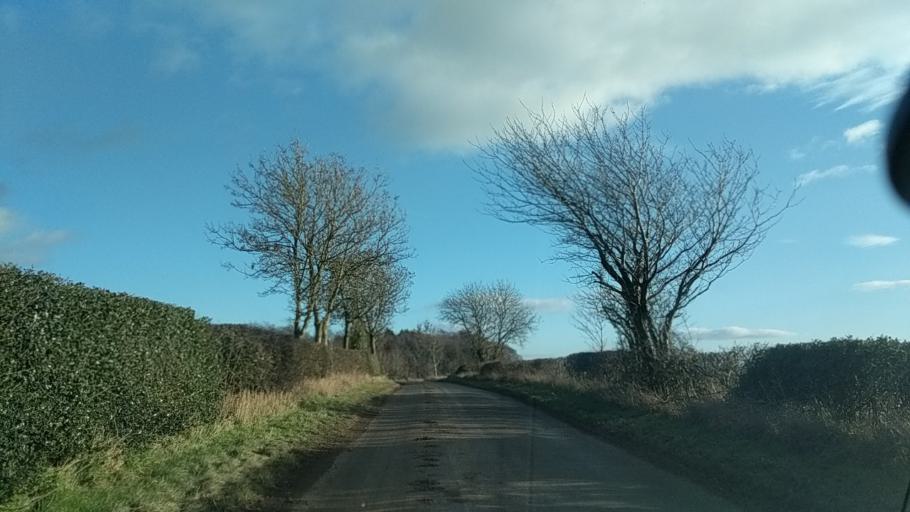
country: GB
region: Scotland
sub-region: West Lothian
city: Broxburn
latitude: 55.9759
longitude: -3.4672
